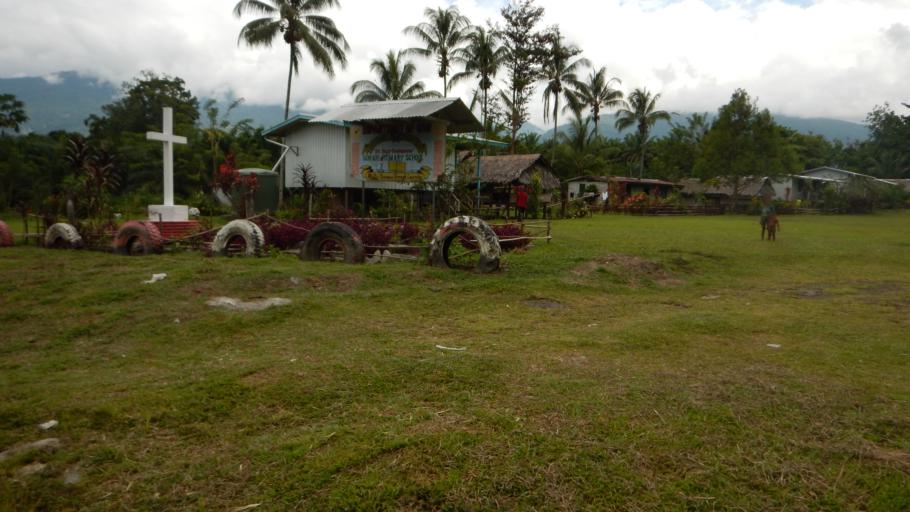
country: PG
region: Northern Province
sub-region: Sohe
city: Kokoda
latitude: -8.9171
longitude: 147.8772
